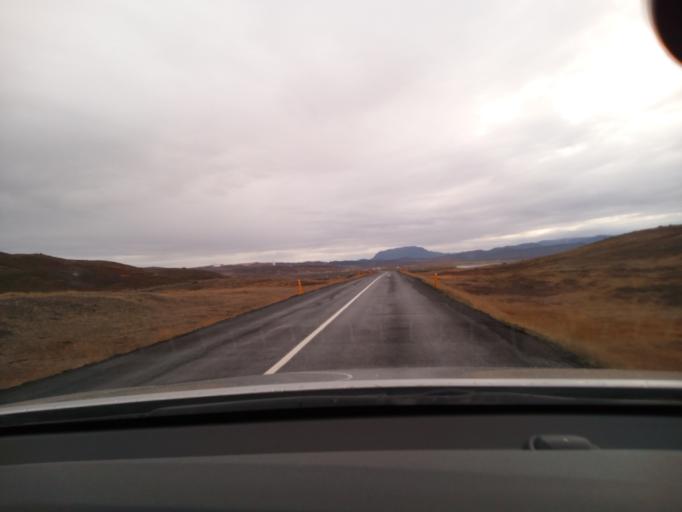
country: IS
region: Northeast
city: Laugar
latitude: 65.6624
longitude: -16.9815
